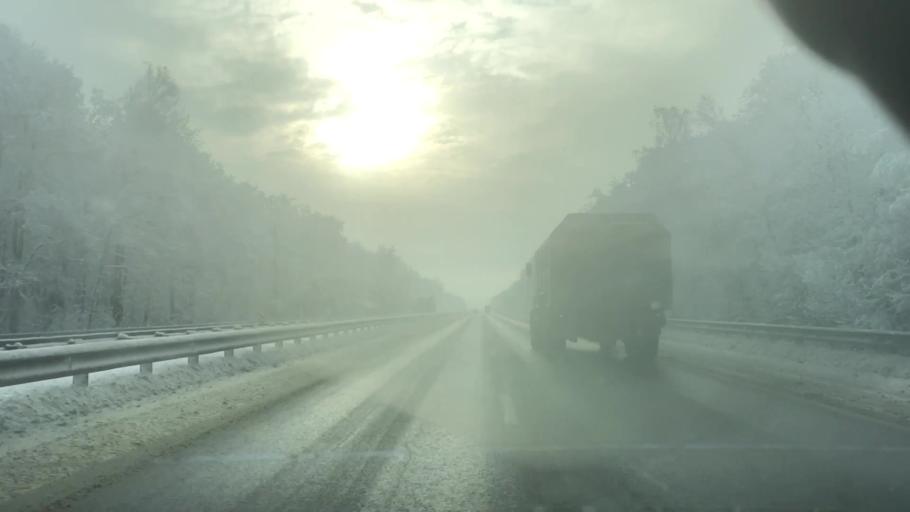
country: RU
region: Tula
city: Venev
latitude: 54.3688
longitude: 38.1547
